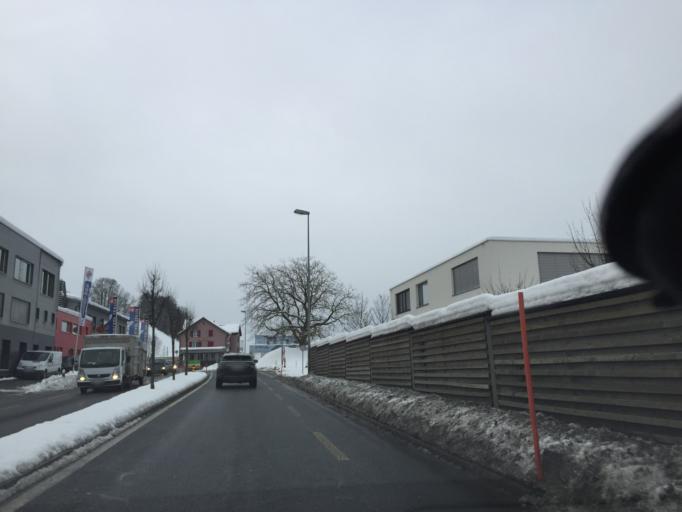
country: CH
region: Schwyz
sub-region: Bezirk Hoefe
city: Schindellegi
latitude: 47.1771
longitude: 8.7107
